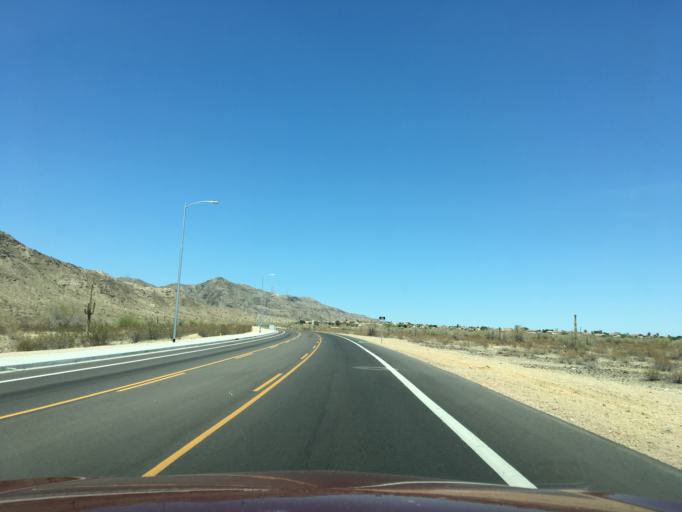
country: US
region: Arizona
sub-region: Maricopa County
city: Laveen
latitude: 33.2982
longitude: -112.1100
